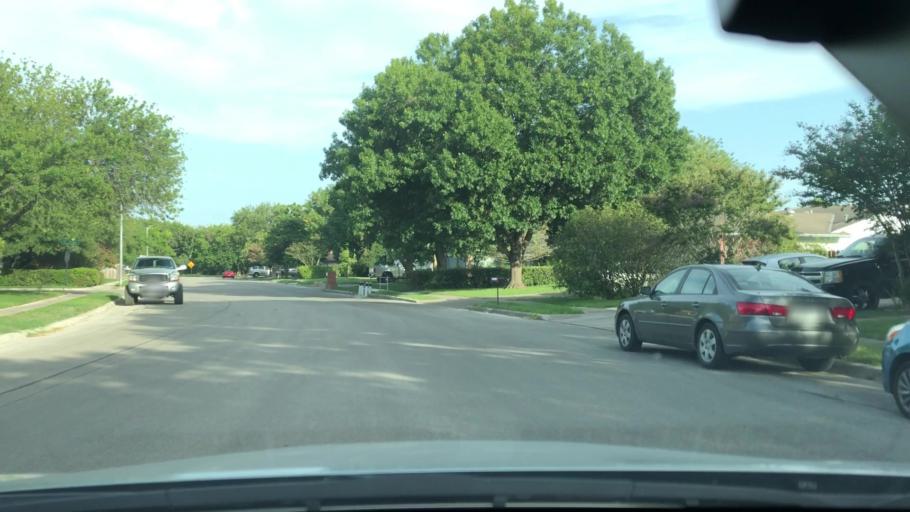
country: US
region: Texas
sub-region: Bexar County
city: Converse
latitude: 29.5343
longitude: -98.3235
